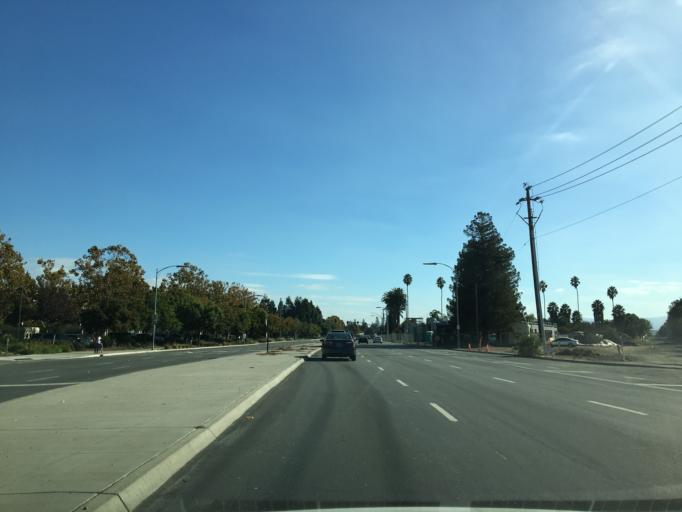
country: US
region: California
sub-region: Santa Clara County
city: Milpitas
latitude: 37.3876
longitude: -121.8994
